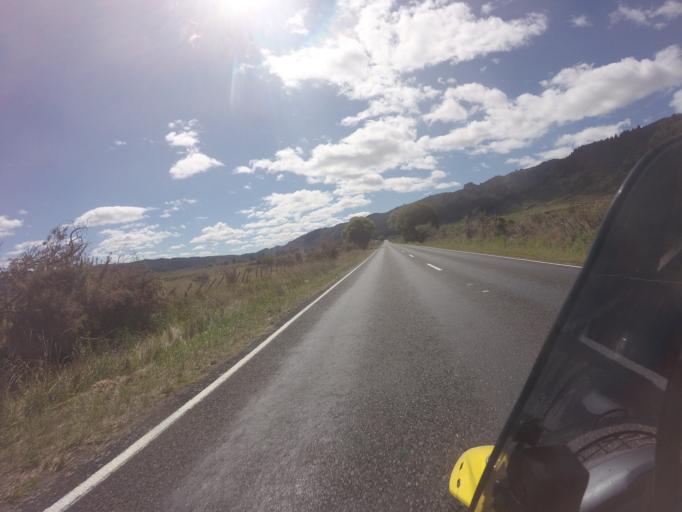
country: NZ
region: Bay of Plenty
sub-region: Kawerau District
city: Kawerau
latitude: -38.2176
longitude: 176.8430
